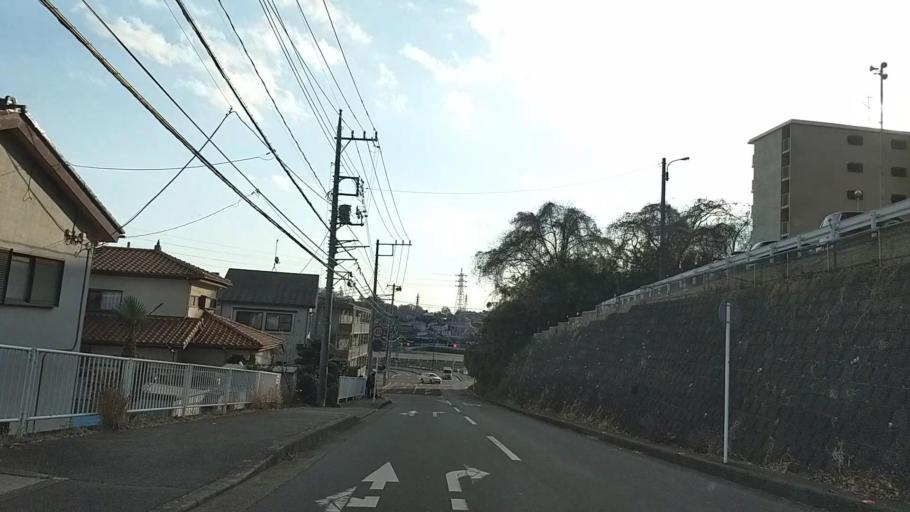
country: JP
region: Kanagawa
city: Atsugi
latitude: 35.4429
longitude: 139.3428
